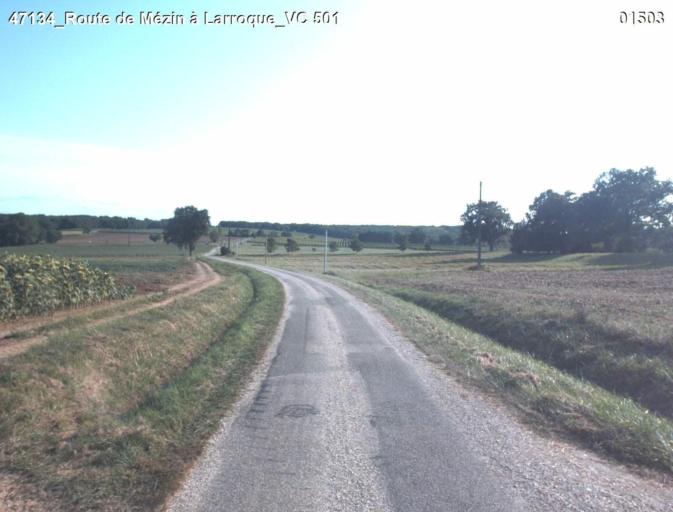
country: FR
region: Aquitaine
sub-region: Departement du Lot-et-Garonne
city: Mezin
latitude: 44.0113
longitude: 0.2763
